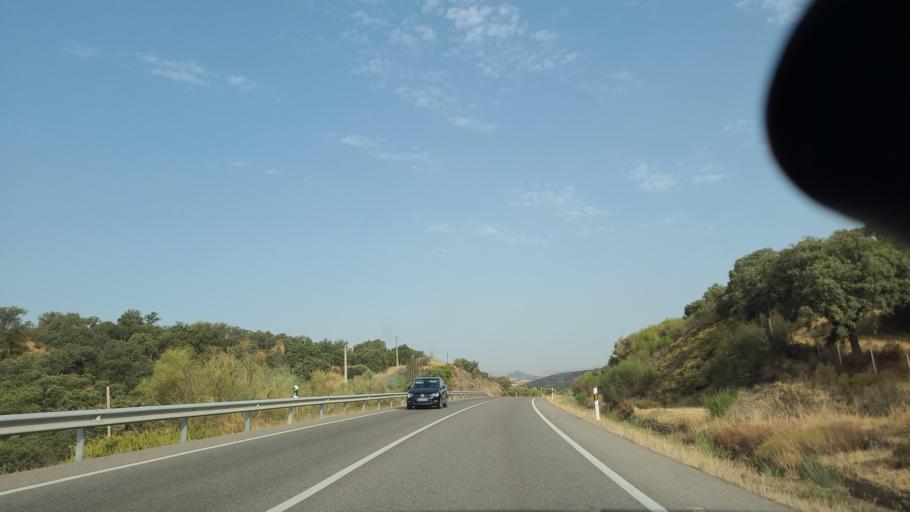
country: ES
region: Andalusia
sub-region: Province of Cordoba
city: Espiel
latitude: 38.1926
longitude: -5.0963
